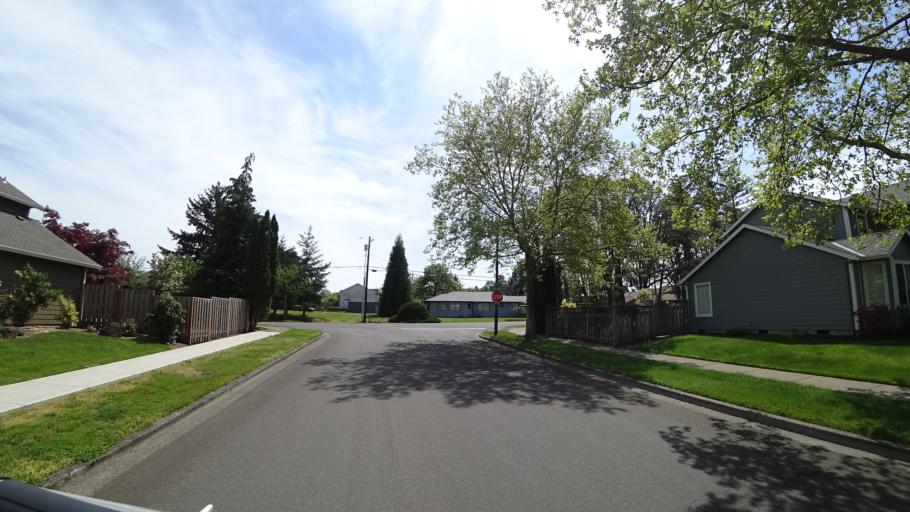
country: US
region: Oregon
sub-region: Washington County
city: Aloha
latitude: 45.5080
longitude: -122.9243
